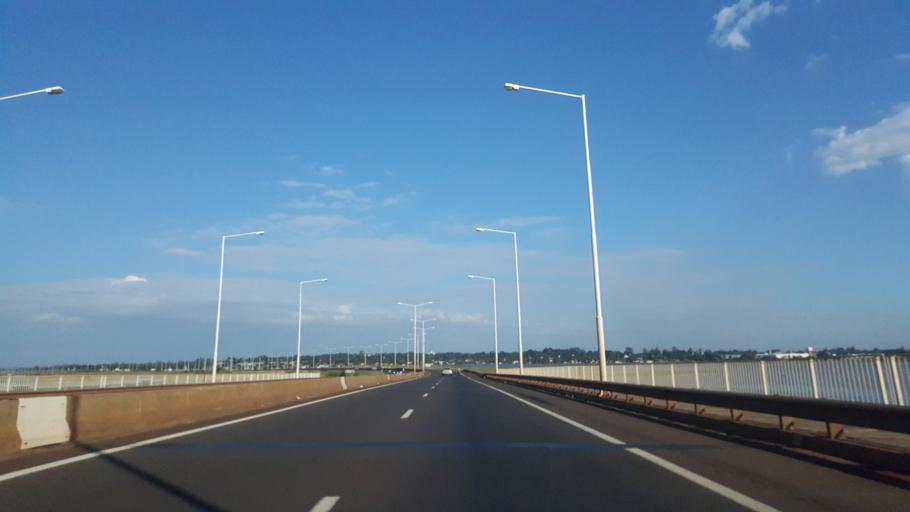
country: AR
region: Misiones
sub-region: Departamento de Capital
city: Posadas
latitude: -27.4062
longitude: -55.8916
